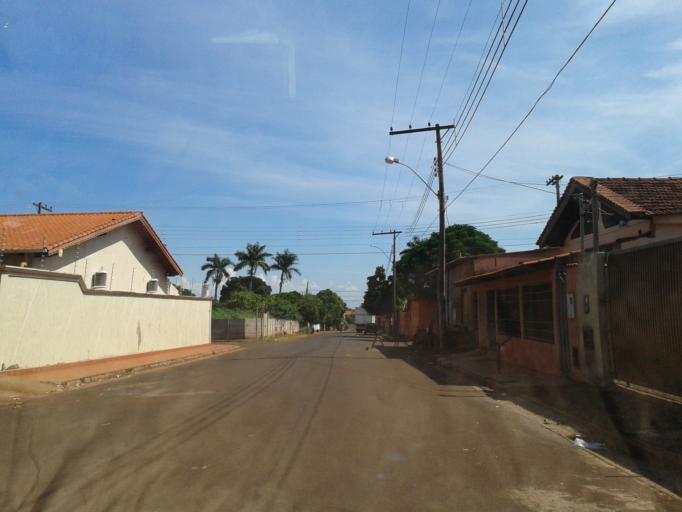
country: BR
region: Minas Gerais
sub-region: Centralina
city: Centralina
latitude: -18.5811
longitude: -49.1941
